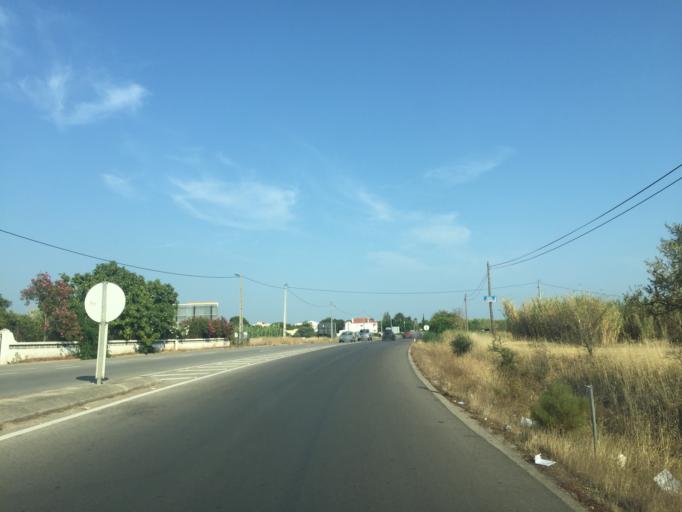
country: PT
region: Faro
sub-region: Loule
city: Almancil
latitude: 37.0954
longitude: -8.0652
